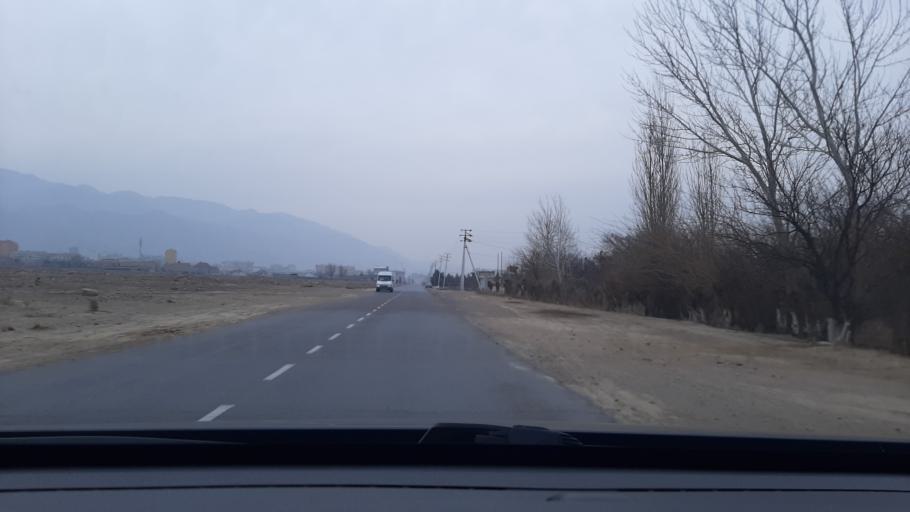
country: TJ
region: Viloyati Sughd
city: Khujand
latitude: 40.2734
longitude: 69.5772
